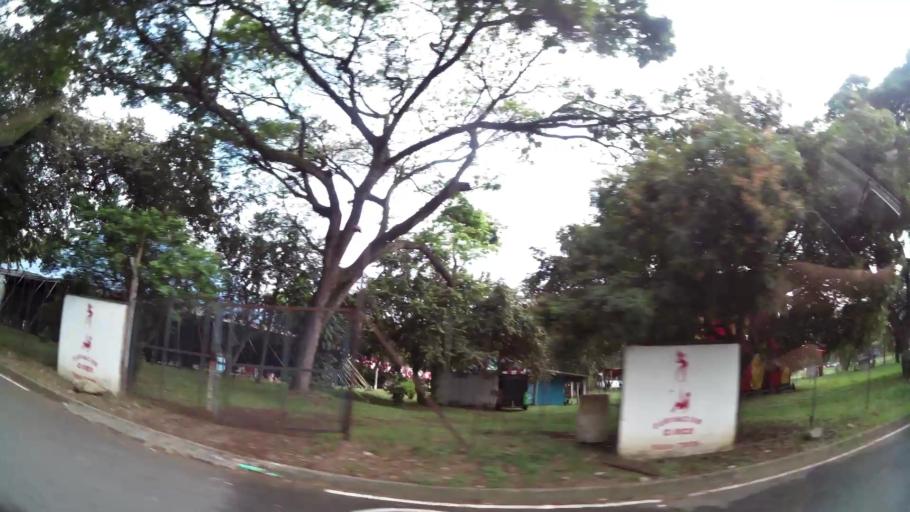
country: CO
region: Valle del Cauca
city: Cali
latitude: 3.4920
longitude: -76.5185
